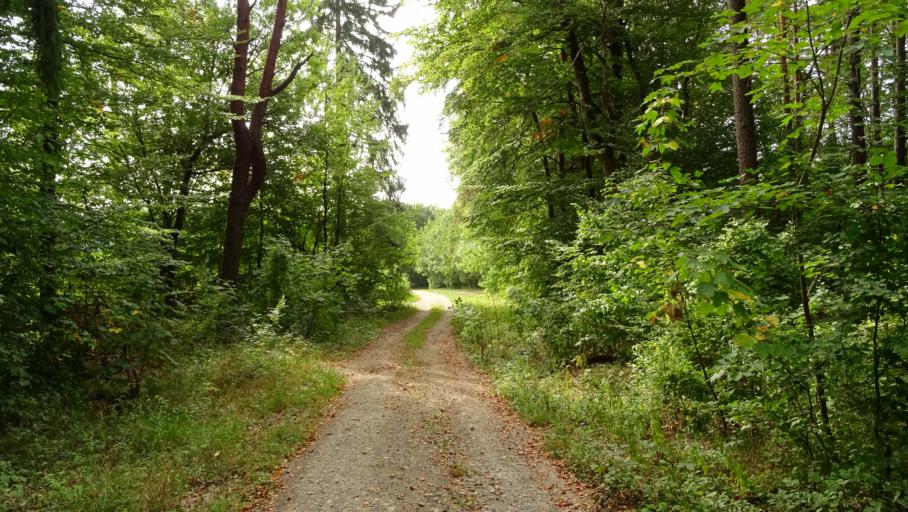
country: DE
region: Baden-Wuerttemberg
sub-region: Karlsruhe Region
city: Mosbach
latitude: 49.3835
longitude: 9.1591
